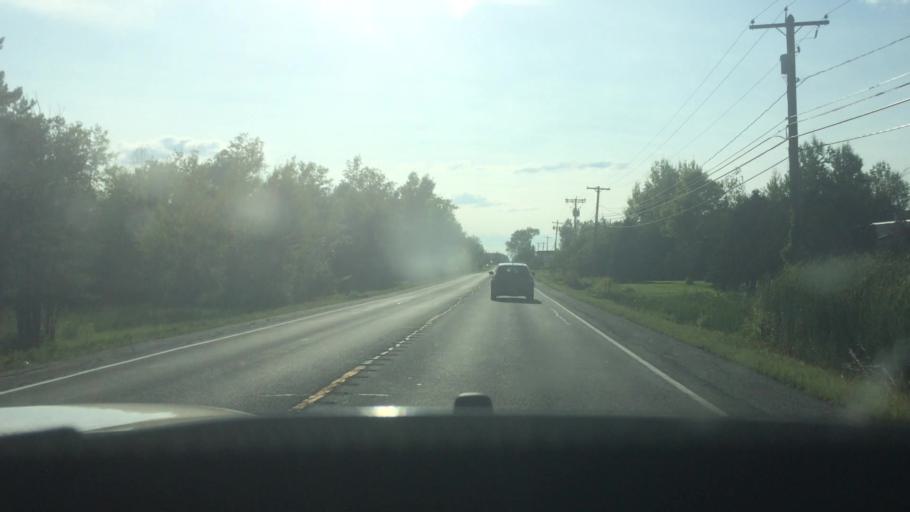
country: US
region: New York
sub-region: St. Lawrence County
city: Potsdam
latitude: 44.6700
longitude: -74.9430
